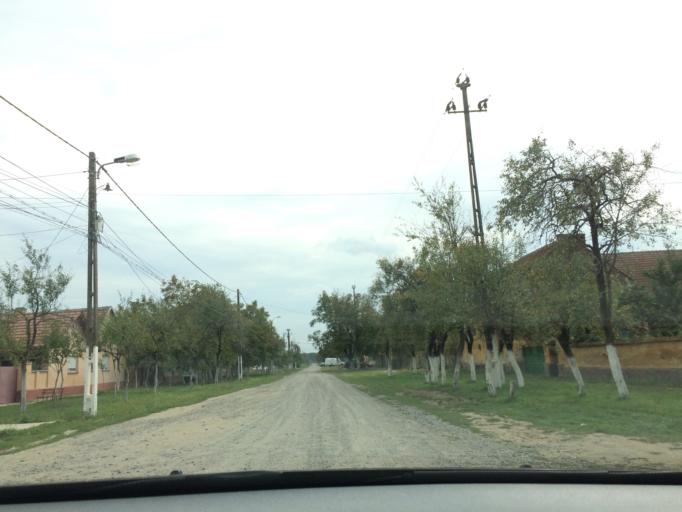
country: RO
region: Timis
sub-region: Oras Recas
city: Recas
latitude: 45.7355
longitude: 21.4919
